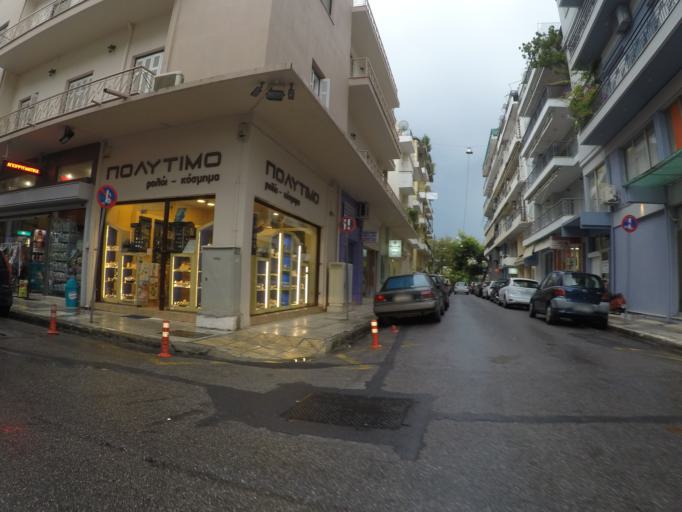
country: GR
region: Peloponnese
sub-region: Nomos Messinias
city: Kalamata
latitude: 37.0389
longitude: 22.1096
